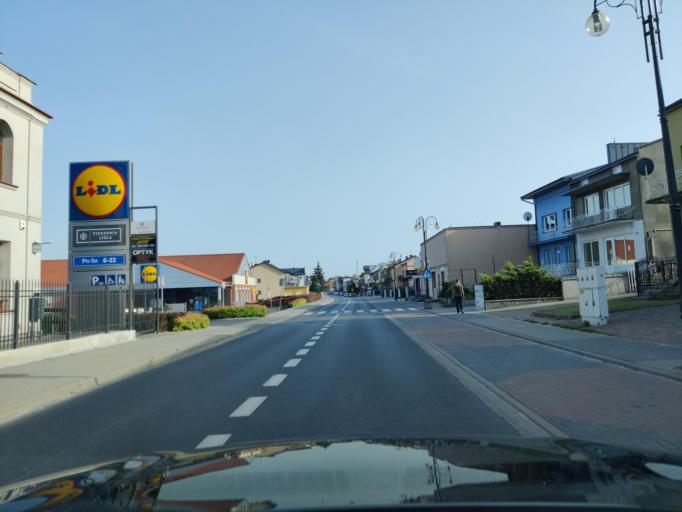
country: PL
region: Masovian Voivodeship
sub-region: Powiat wyszkowski
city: Wyszkow
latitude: 52.5990
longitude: 21.4564
